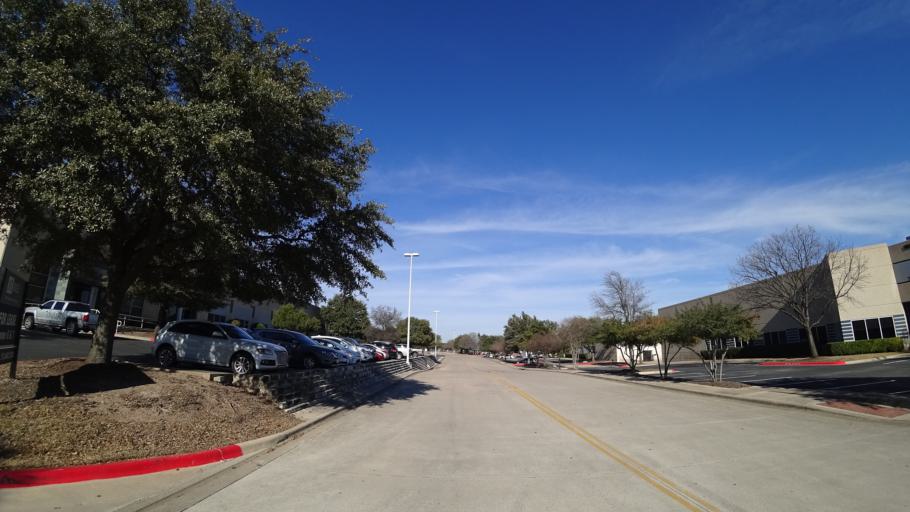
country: US
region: Texas
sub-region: Travis County
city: Wells Branch
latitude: 30.3853
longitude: -97.7103
